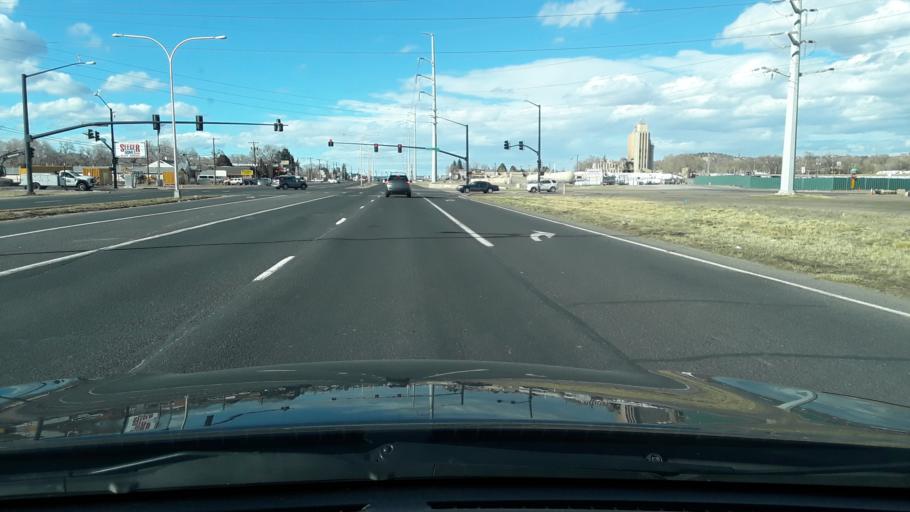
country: US
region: Colorado
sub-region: El Paso County
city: Colorado Springs
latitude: 38.8851
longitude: -104.8188
